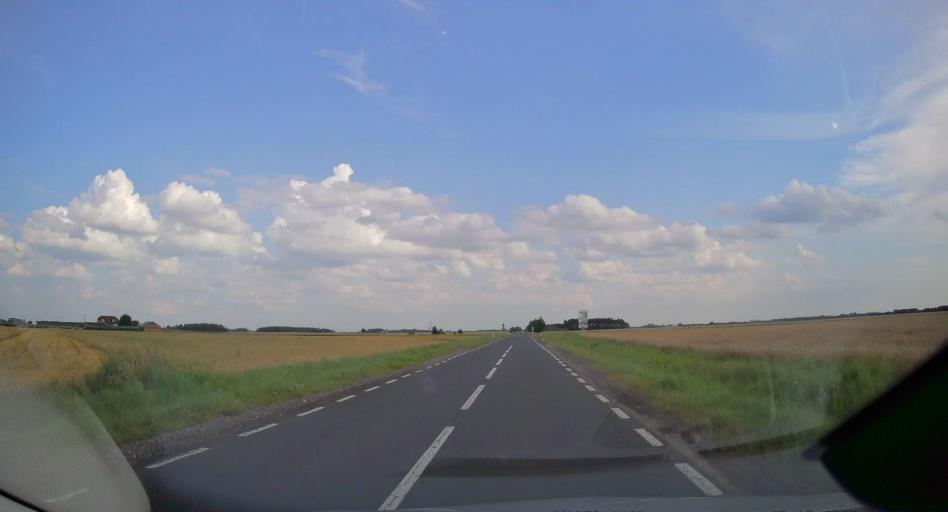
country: PL
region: Lodz Voivodeship
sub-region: Powiat tomaszowski
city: Rzeczyca
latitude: 51.6673
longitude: 20.2640
